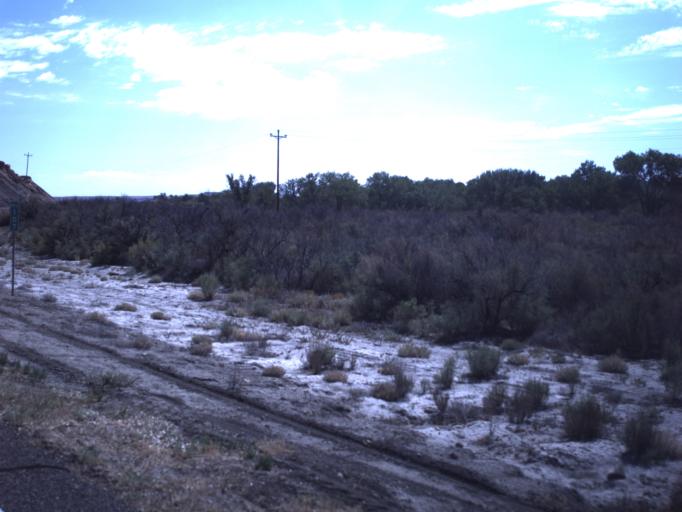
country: US
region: Utah
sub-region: Wayne County
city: Loa
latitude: 38.3607
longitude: -110.8700
